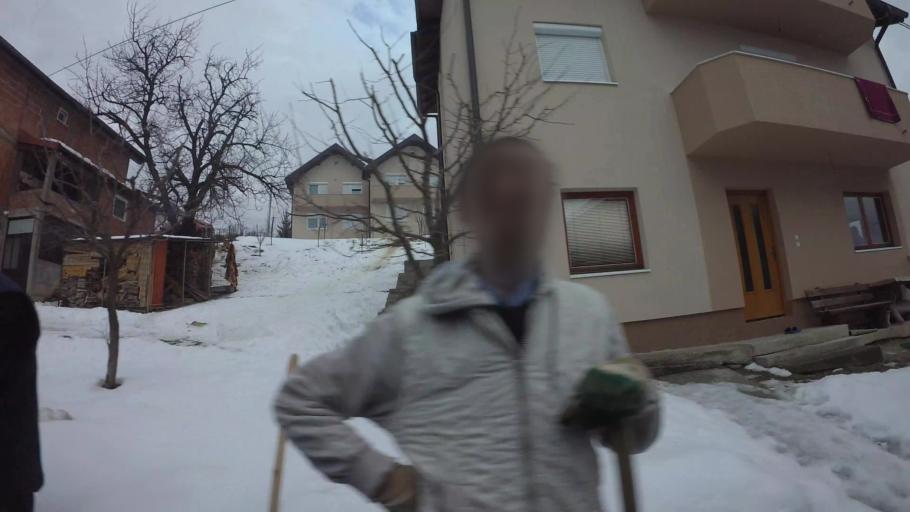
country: BA
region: Federation of Bosnia and Herzegovina
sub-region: Kanton Sarajevo
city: Sarajevo
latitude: 43.8589
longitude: 18.3519
